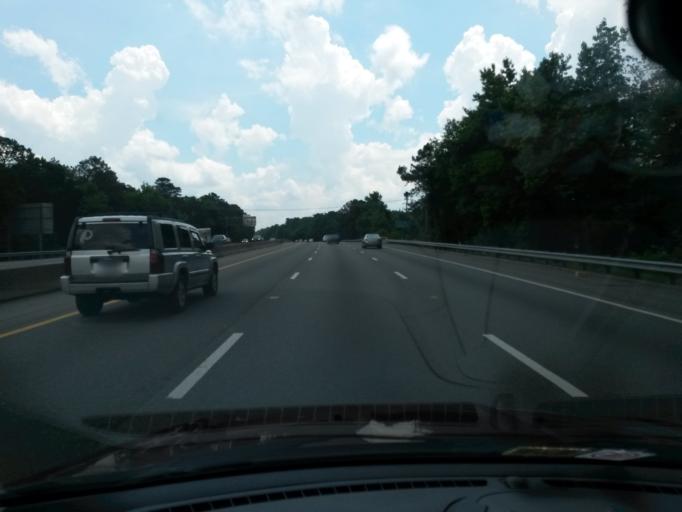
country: US
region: Virginia
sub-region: Chesterfield County
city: Bellwood
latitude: 37.3920
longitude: -77.4227
